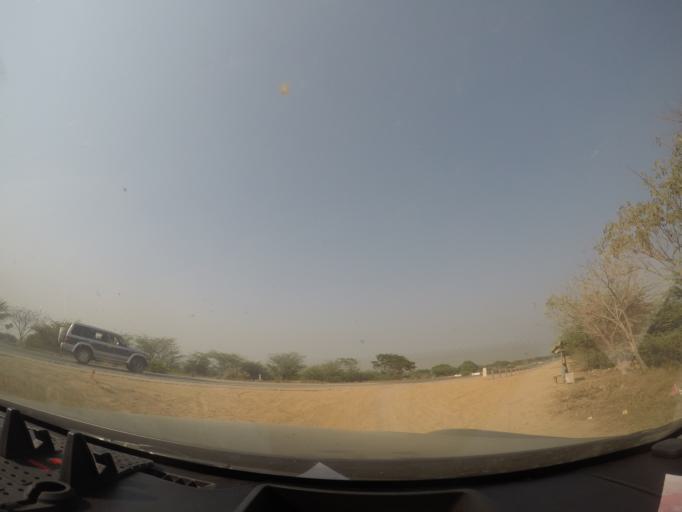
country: MM
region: Sagain
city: Sagaing
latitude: 21.8609
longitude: 96.0285
